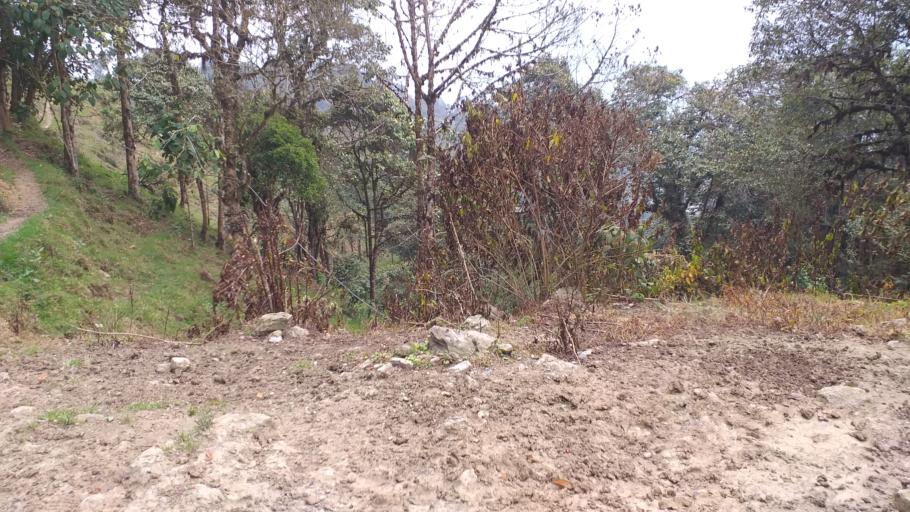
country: CO
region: Boyaca
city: Aquitania
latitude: 5.3288
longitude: -72.9308
